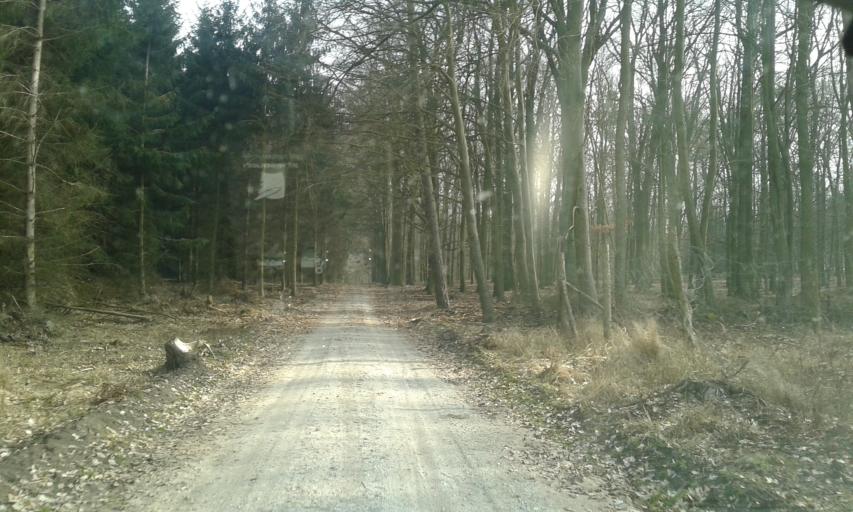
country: PL
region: West Pomeranian Voivodeship
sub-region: Powiat choszczenski
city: Pelczyce
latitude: 53.0827
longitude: 15.2569
